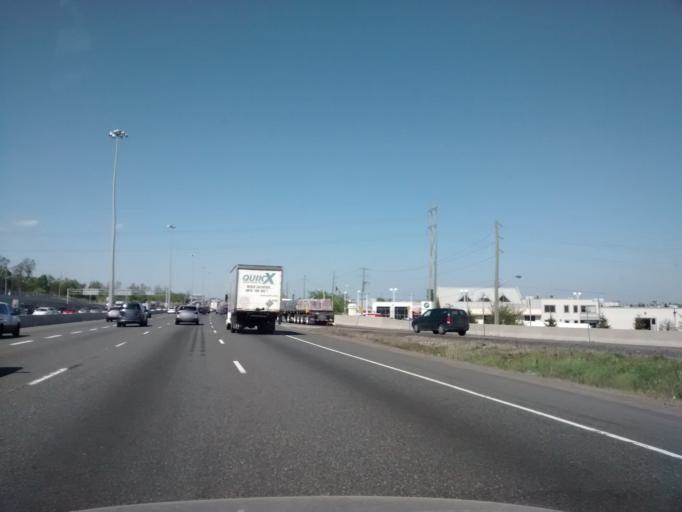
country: CA
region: Ontario
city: Oakville
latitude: 43.4116
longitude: -79.7385
